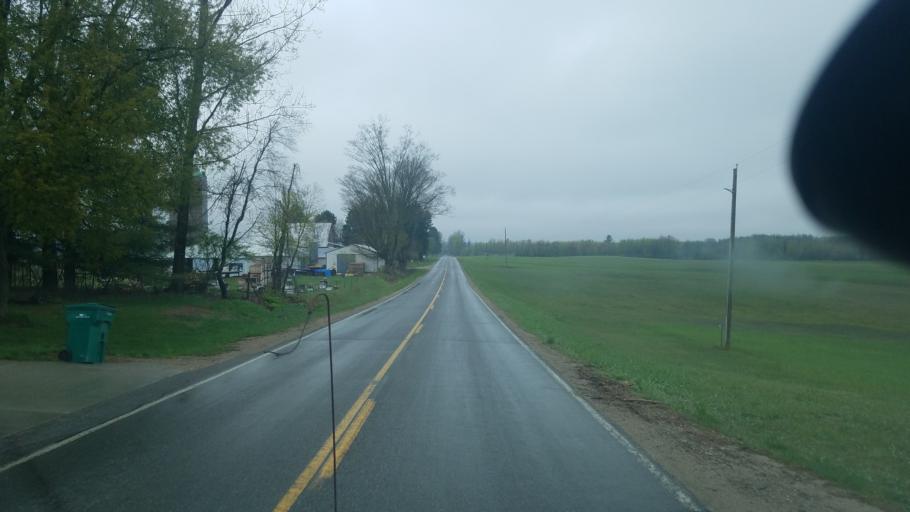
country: US
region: Michigan
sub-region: Mecosta County
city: Canadian Lakes
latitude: 43.5798
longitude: -85.3936
